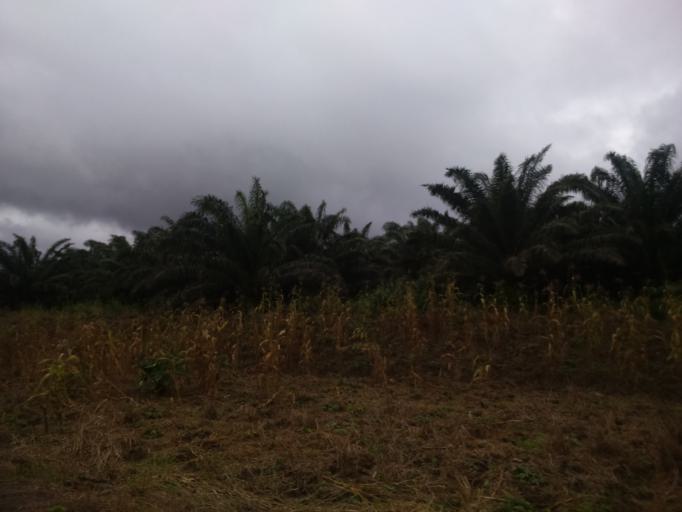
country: CI
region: Sud-Comoe
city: Adiake
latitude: 5.3004
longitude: -3.3491
